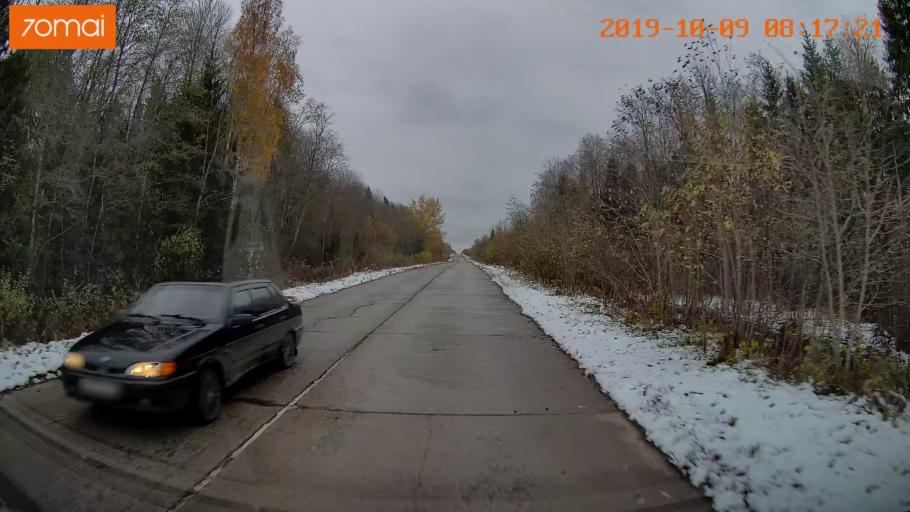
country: RU
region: Vologda
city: Gryazovets
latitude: 58.7385
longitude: 40.2040
